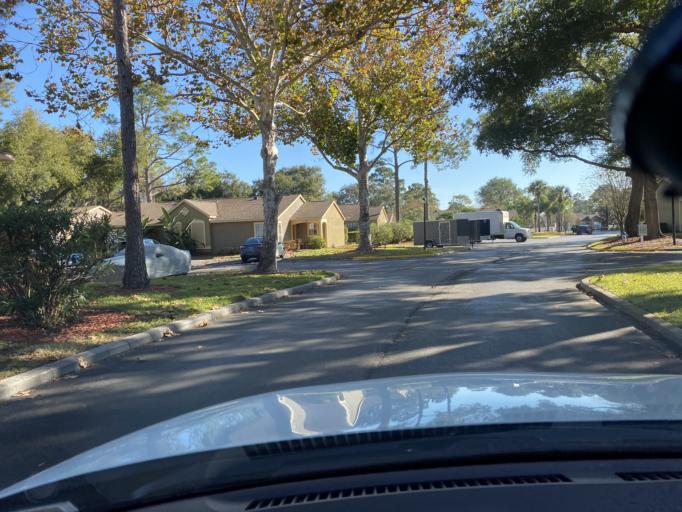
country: US
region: Florida
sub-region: Orange County
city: Azalea Park
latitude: 28.5183
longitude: -81.3075
